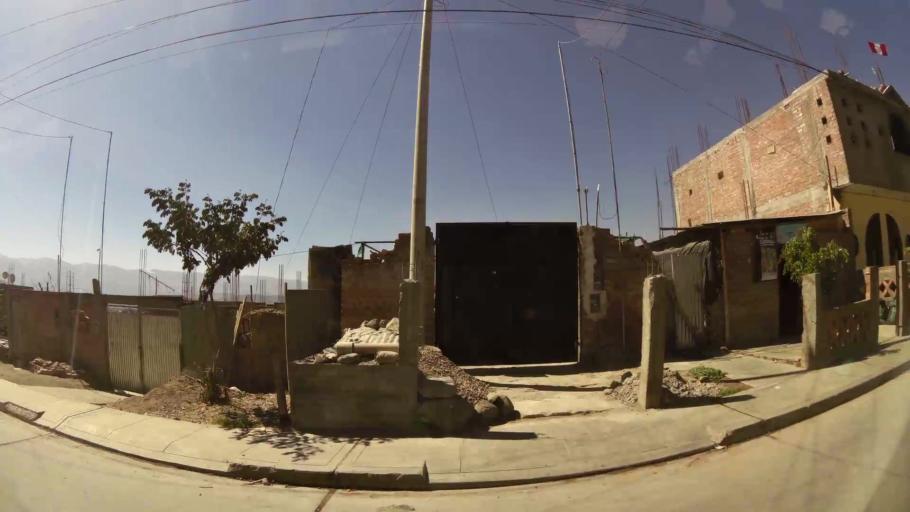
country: PE
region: Ayacucho
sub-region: Provincia de Huamanga
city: Ayacucho
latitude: -13.1530
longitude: -74.2326
